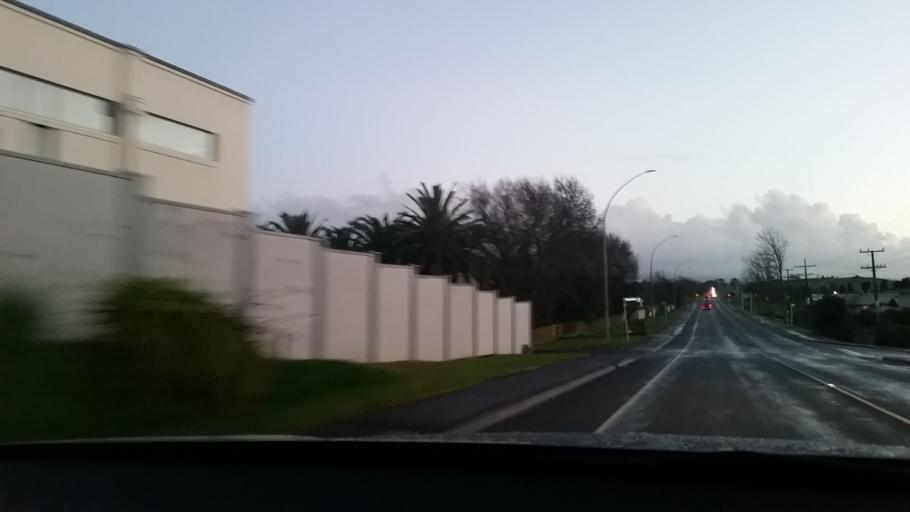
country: NZ
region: Waikato
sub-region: Hamilton City
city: Hamilton
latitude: -37.8046
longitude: 175.2426
